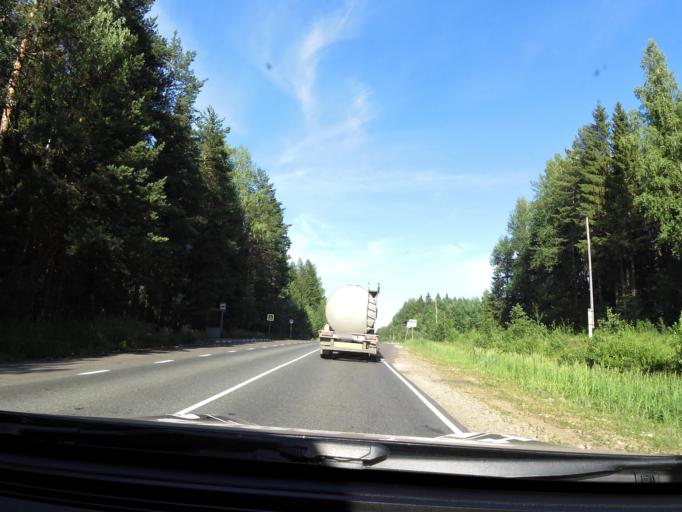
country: RU
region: Kirov
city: Belaya Kholunitsa
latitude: 58.9044
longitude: 50.9574
